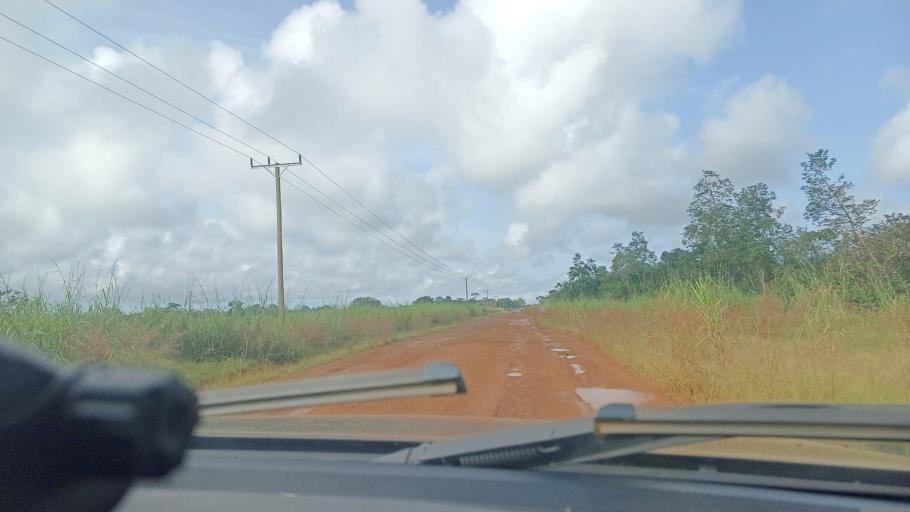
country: LR
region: Grand Cape Mount
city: Robertsport
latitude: 6.6918
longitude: -11.1104
